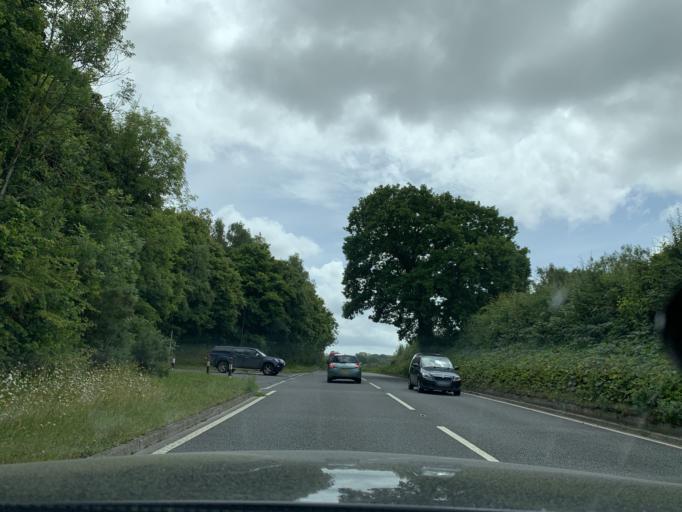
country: GB
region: England
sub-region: East Sussex
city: Robertsbridge
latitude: 50.9757
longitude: 0.4749
